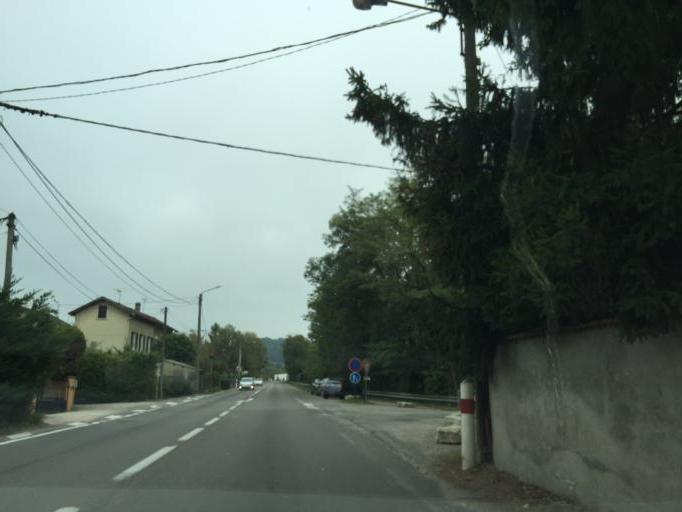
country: FR
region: Rhone-Alpes
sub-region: Departement de l'Isere
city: La Tour-du-Pin
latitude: 45.5693
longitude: 5.4585
